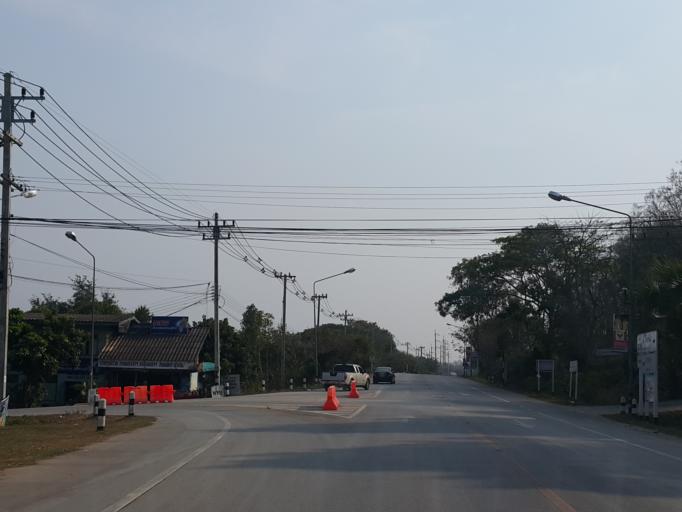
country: TH
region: Lampang
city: Chae Hom
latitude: 18.7058
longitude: 99.5550
